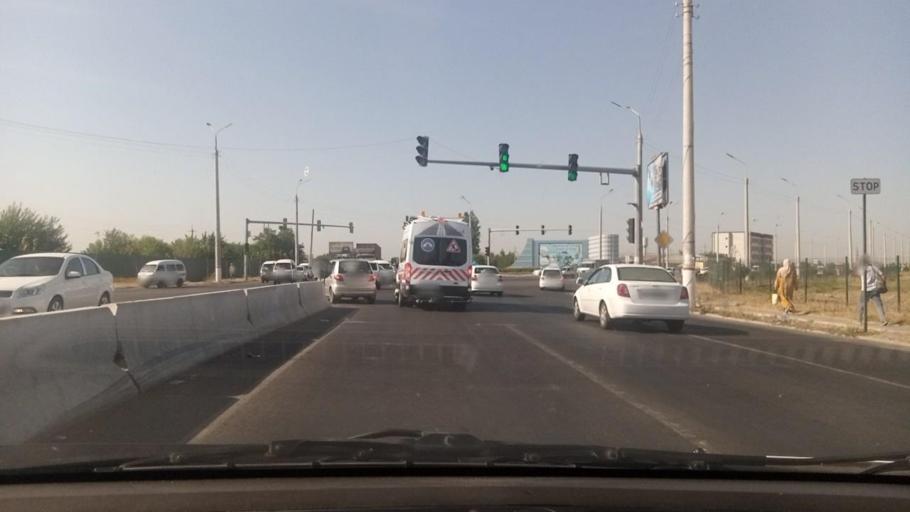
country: UZ
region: Toshkent Shahri
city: Bektemir
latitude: 41.2025
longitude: 69.3324
